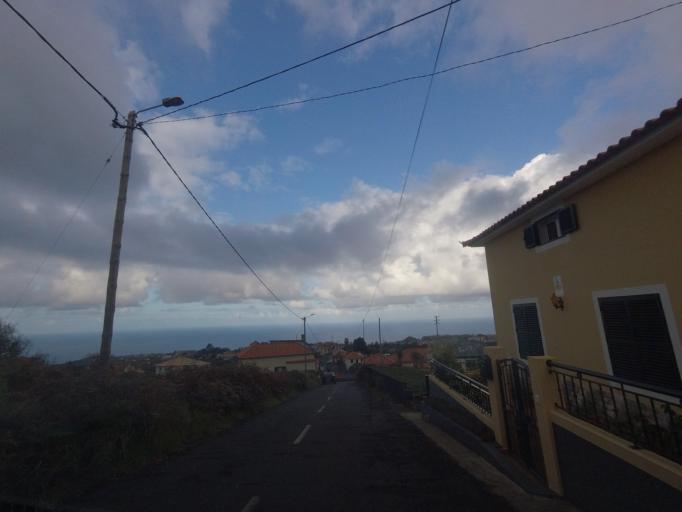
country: PT
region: Madeira
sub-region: Santana
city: Santana
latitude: 32.8038
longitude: -16.8864
